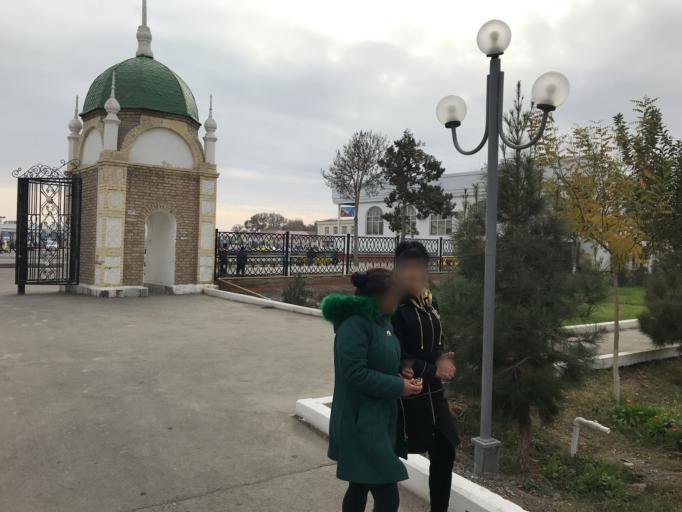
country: UZ
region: Bukhara
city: Kogon
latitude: 39.7235
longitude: 64.5464
